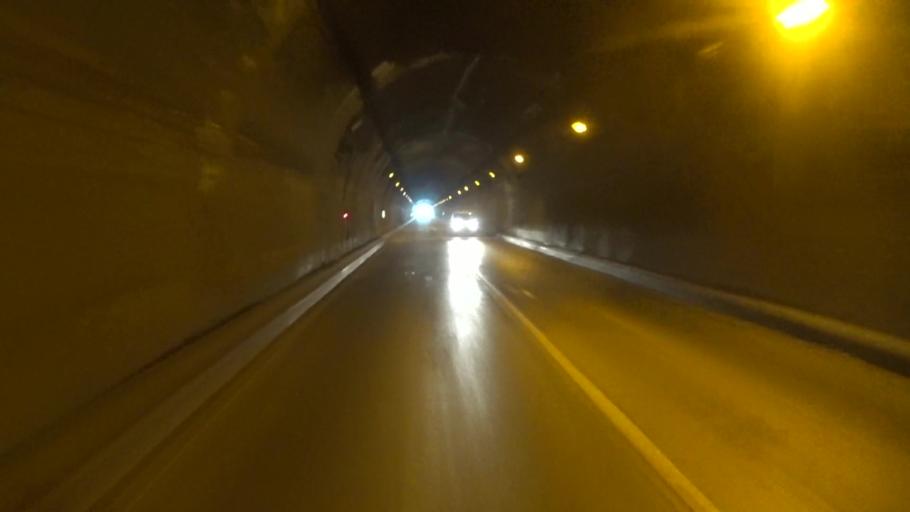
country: JP
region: Kyoto
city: Miyazu
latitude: 35.5517
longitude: 135.2207
